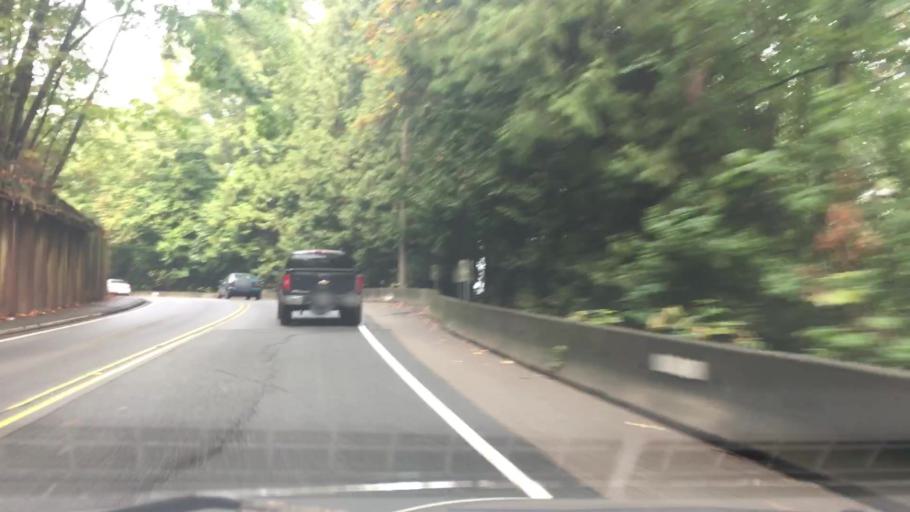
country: CA
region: British Columbia
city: Langley
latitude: 49.1031
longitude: -122.5510
